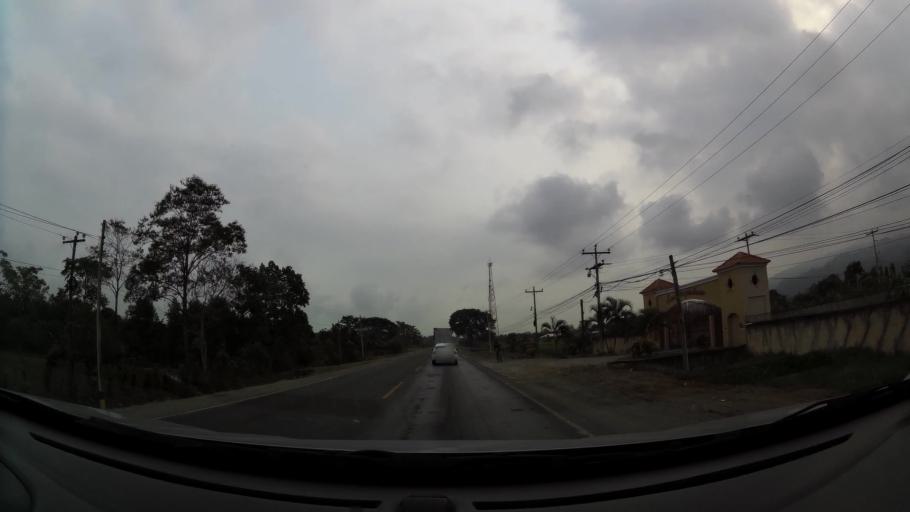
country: HN
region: Yoro
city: El Progreso
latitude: 15.4504
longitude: -87.7884
